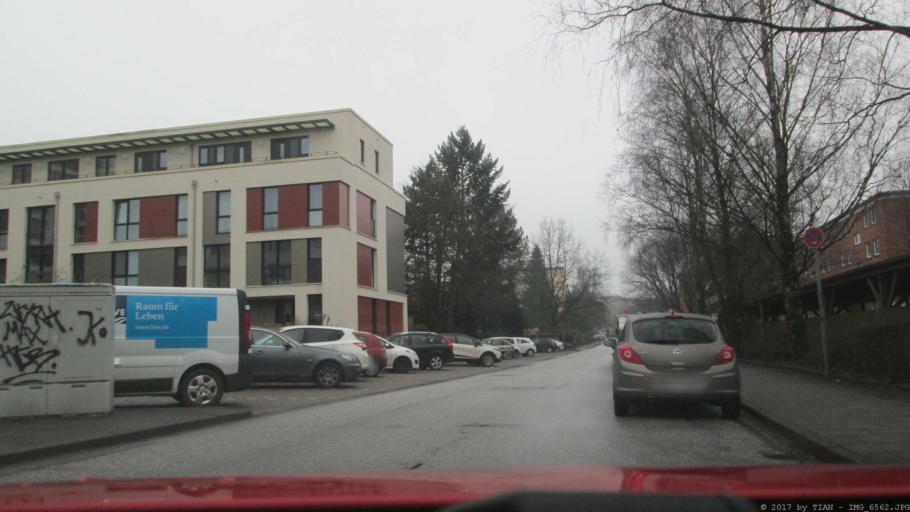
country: DE
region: Schleswig-Holstein
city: Halstenbek
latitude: 53.5829
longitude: 9.8290
